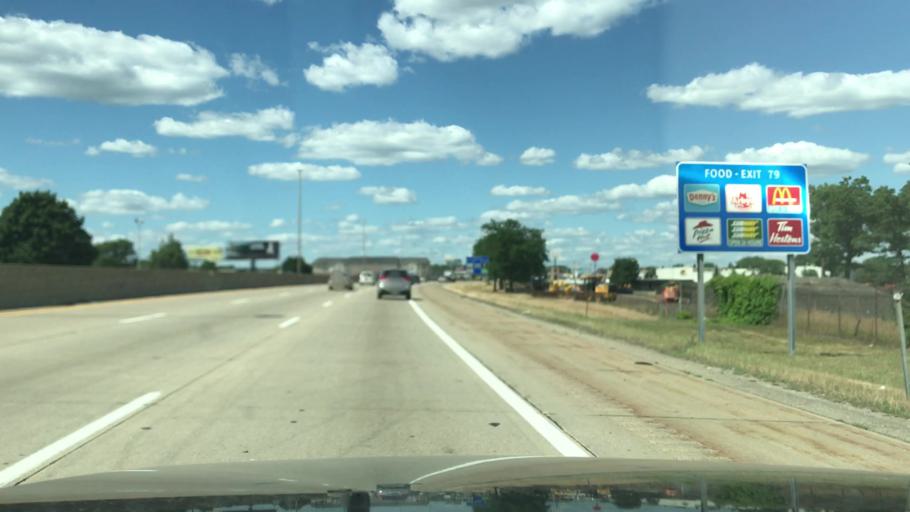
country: US
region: Michigan
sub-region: Kent County
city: Kentwood
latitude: 42.8765
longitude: -85.6819
